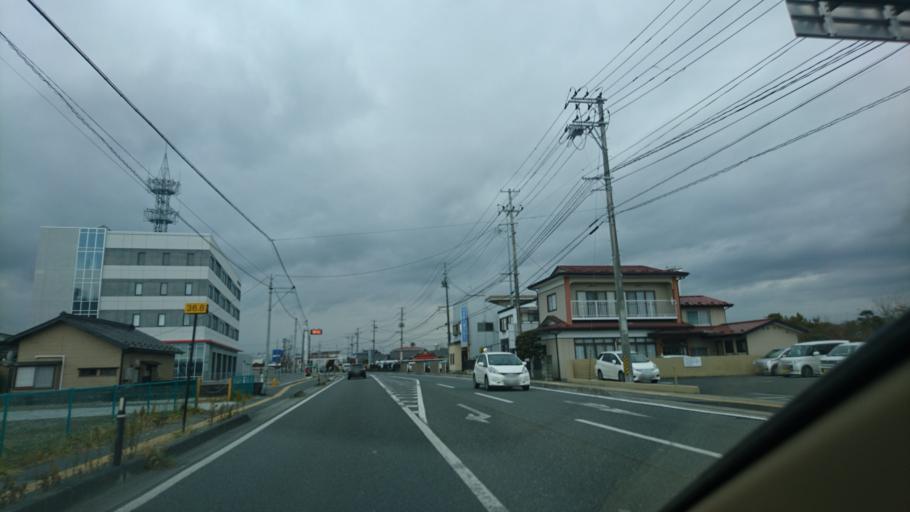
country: JP
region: Miyagi
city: Furukawa
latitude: 38.5808
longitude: 140.9578
